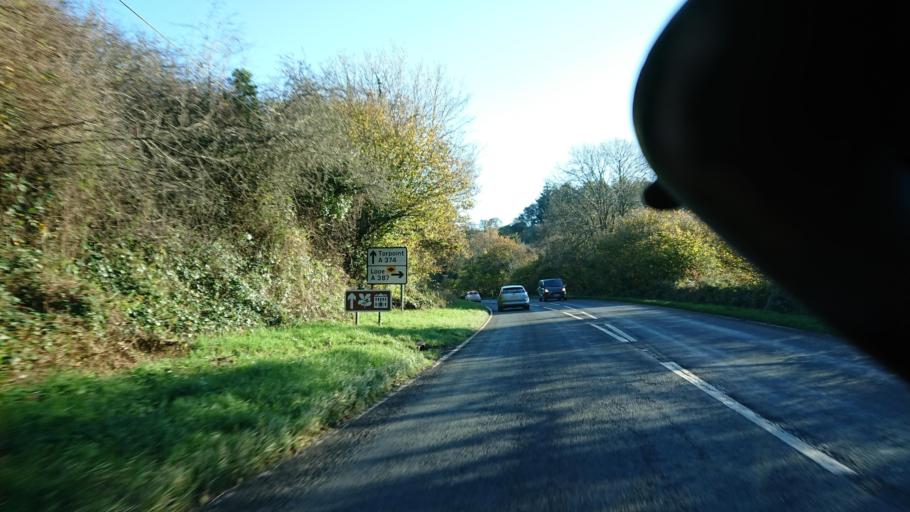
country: GB
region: England
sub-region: Cornwall
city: Pillaton
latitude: 50.3927
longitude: -4.3442
